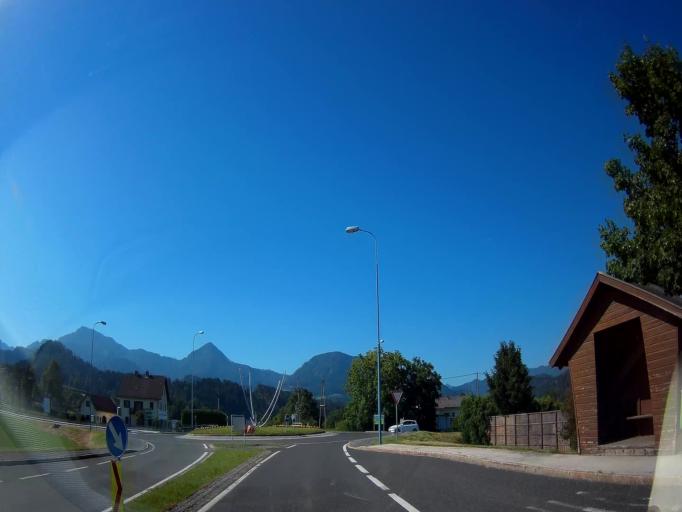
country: AT
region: Carinthia
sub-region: Politischer Bezirk Volkermarkt
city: Eberndorf
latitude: 46.5774
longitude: 14.6263
